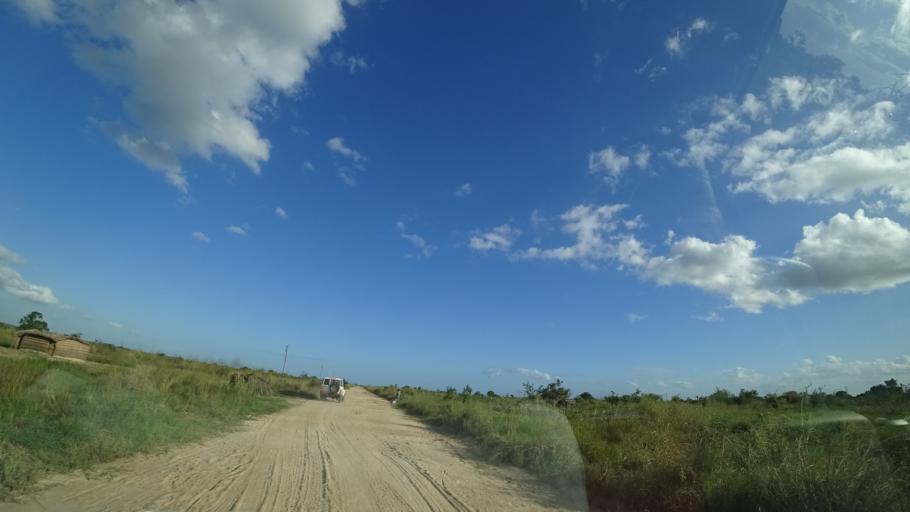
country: MZ
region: Sofala
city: Dondo
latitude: -19.4453
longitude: 34.5621
